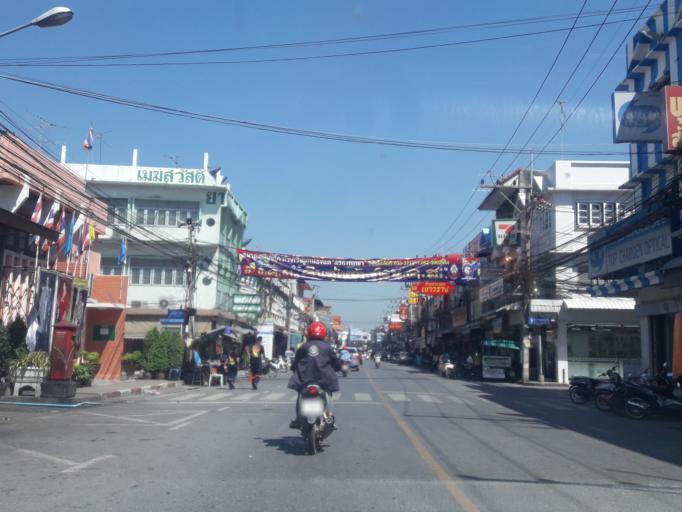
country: TH
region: Sara Buri
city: Nong Khae
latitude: 14.3412
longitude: 100.8669
